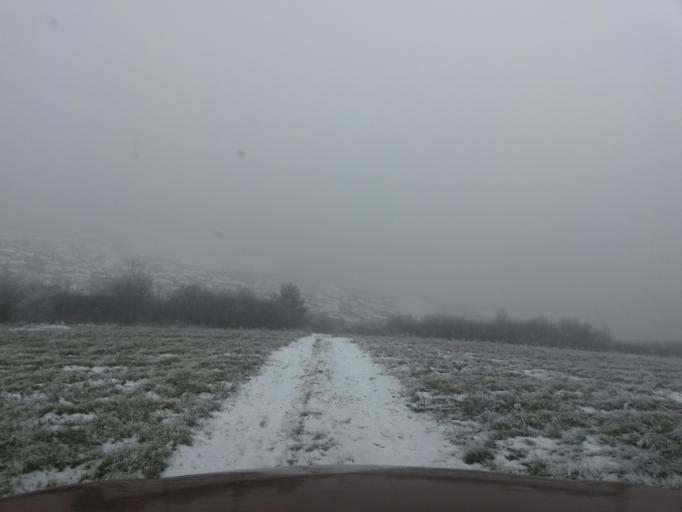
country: SK
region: Kosicky
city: Krompachy
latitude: 48.9697
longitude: 20.9778
